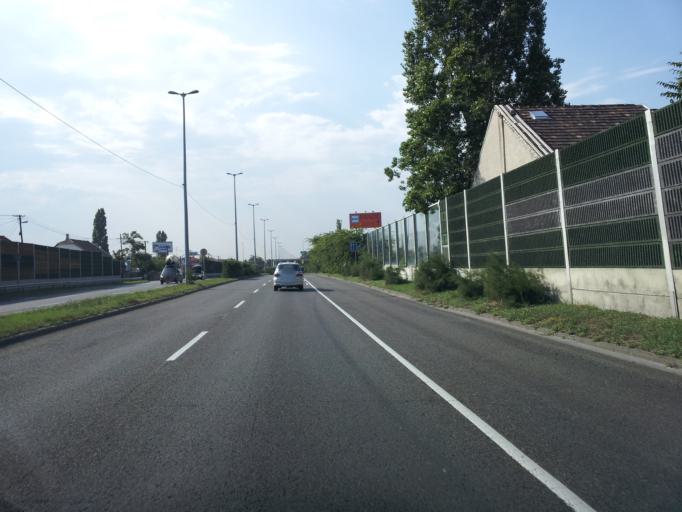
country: HU
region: Budapest
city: Budapest XIX. keruelet
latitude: 47.4442
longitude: 19.1299
